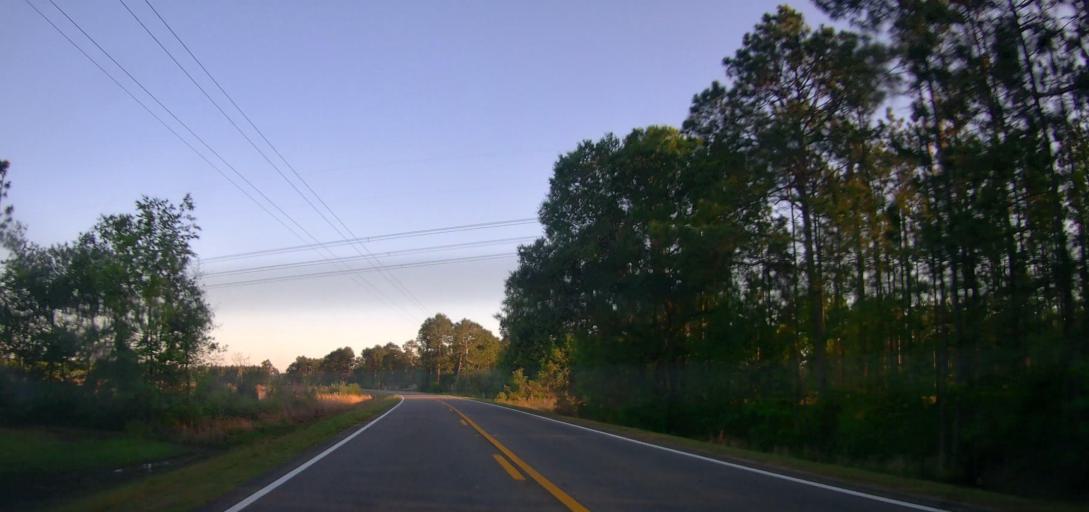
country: US
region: Georgia
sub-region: Irwin County
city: Ocilla
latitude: 31.6235
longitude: -83.2718
